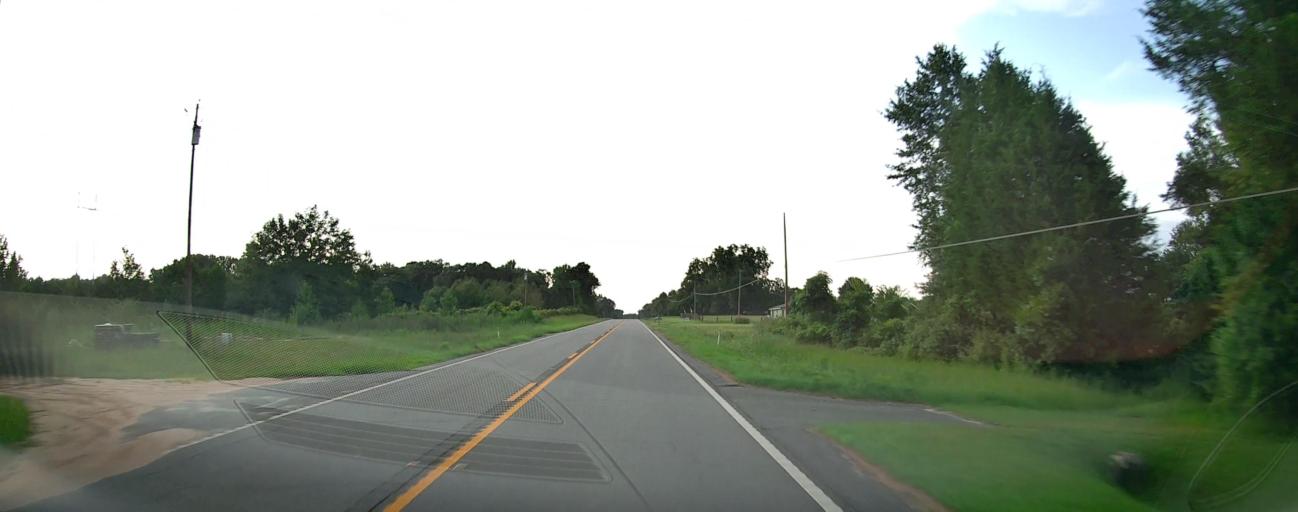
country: US
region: Georgia
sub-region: Taylor County
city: Reynolds
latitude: 32.6073
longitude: -84.0964
